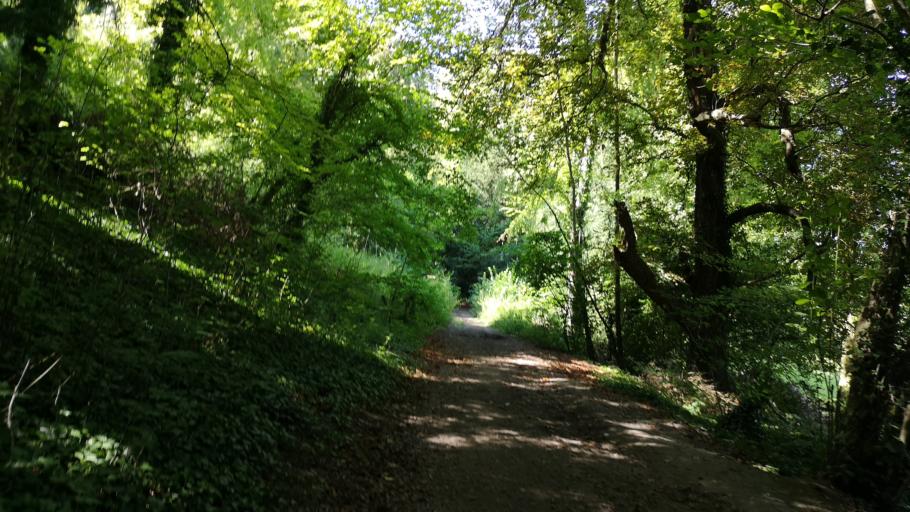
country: GB
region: England
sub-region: Isle of Wight
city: Brading
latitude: 50.6810
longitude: -1.1576
